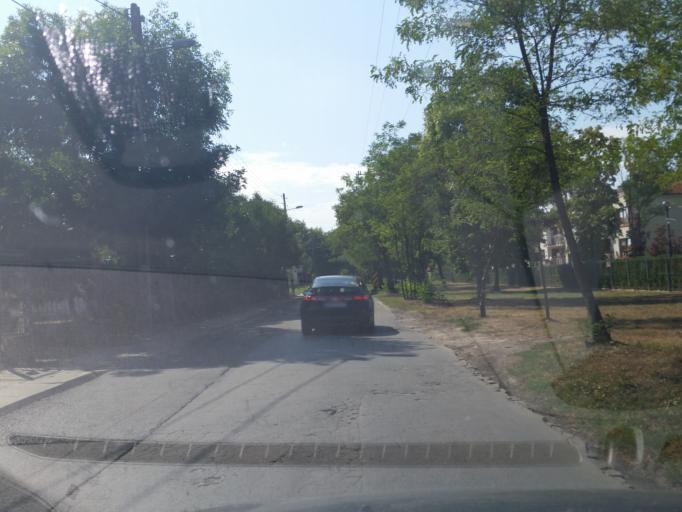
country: PL
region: Masovian Voivodeship
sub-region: Warszawa
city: Bialoleka
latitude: 52.3239
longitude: 20.9788
